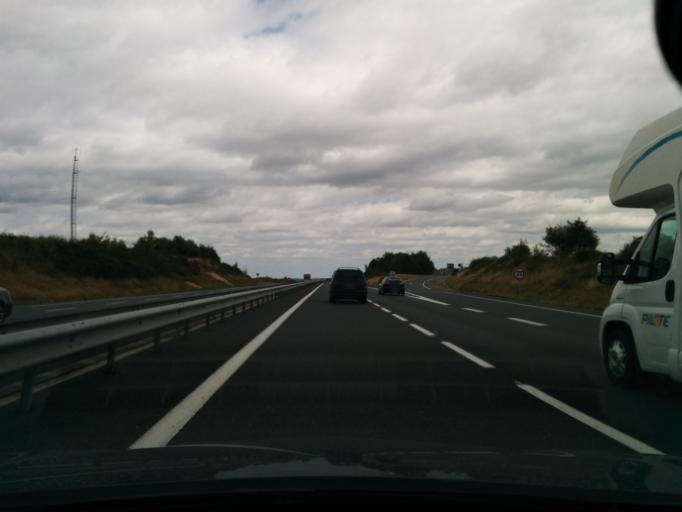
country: FR
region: Centre
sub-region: Departement de l'Indre
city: Argenton-sur-Creuse
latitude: 46.5445
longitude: 1.5064
